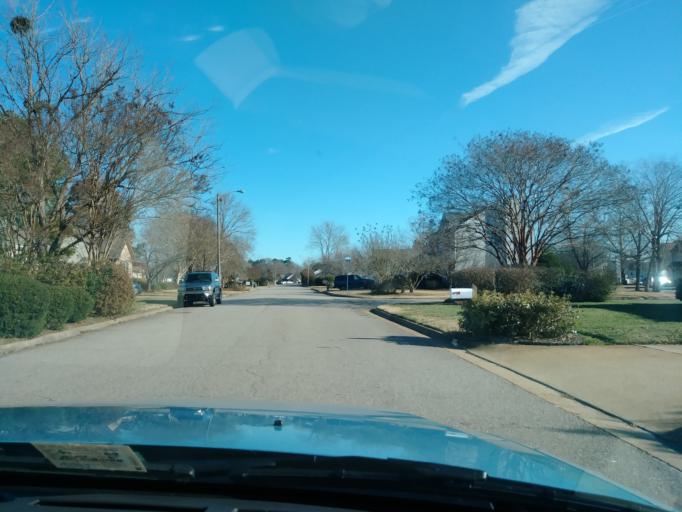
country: US
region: Virginia
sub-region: City of Chesapeake
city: Chesapeake
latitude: 36.7556
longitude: -76.2115
